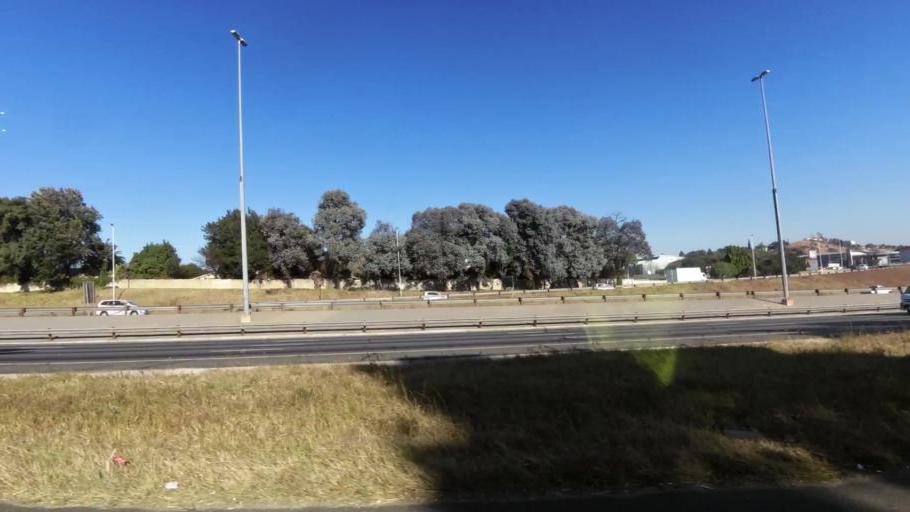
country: ZA
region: Gauteng
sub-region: City of Johannesburg Metropolitan Municipality
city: Roodepoort
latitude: -26.1675
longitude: 27.9417
